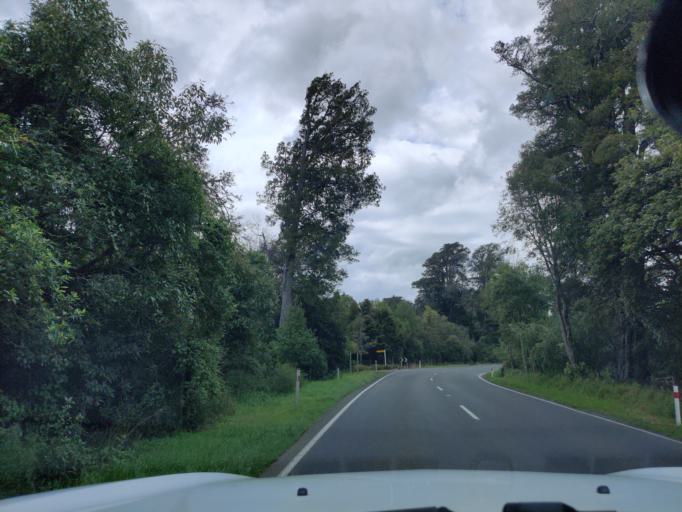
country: NZ
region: Manawatu-Wanganui
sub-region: Palmerston North City
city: Palmerston North
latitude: -40.2469
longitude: 175.5390
